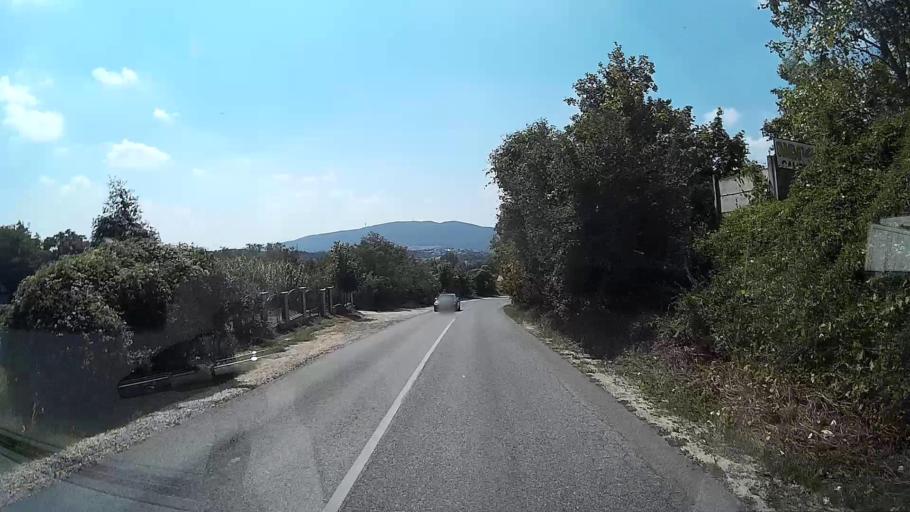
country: HU
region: Pest
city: Urom
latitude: 47.6020
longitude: 19.0207
